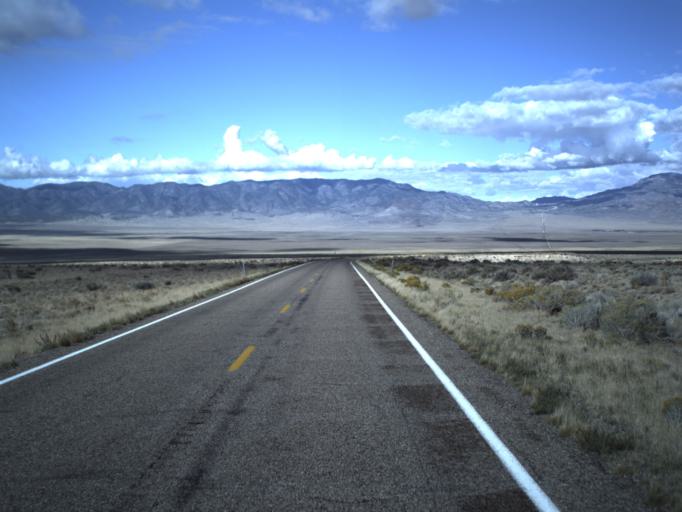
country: US
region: Utah
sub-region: Beaver County
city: Milford
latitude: 38.4363
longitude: -113.3039
